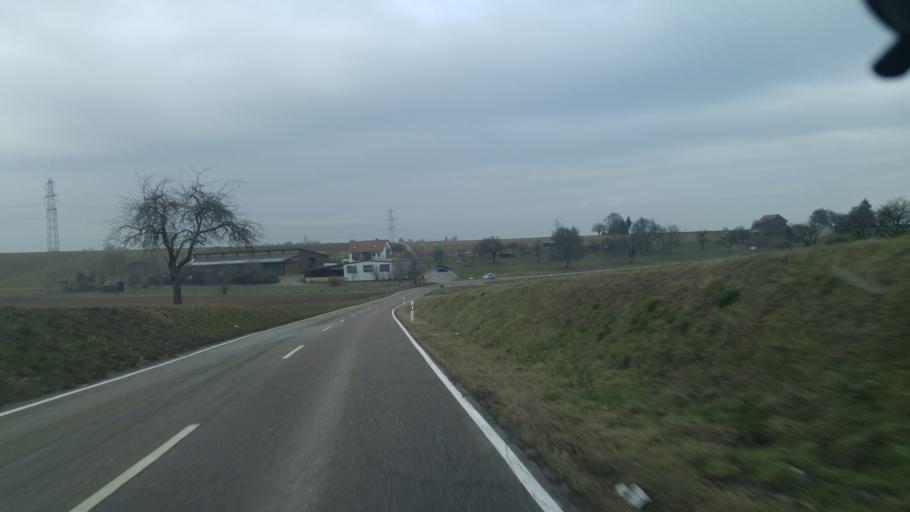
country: DE
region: Baden-Wuerttemberg
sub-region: Regierungsbezirk Stuttgart
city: Leonberg
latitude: 48.8214
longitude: 9.0173
